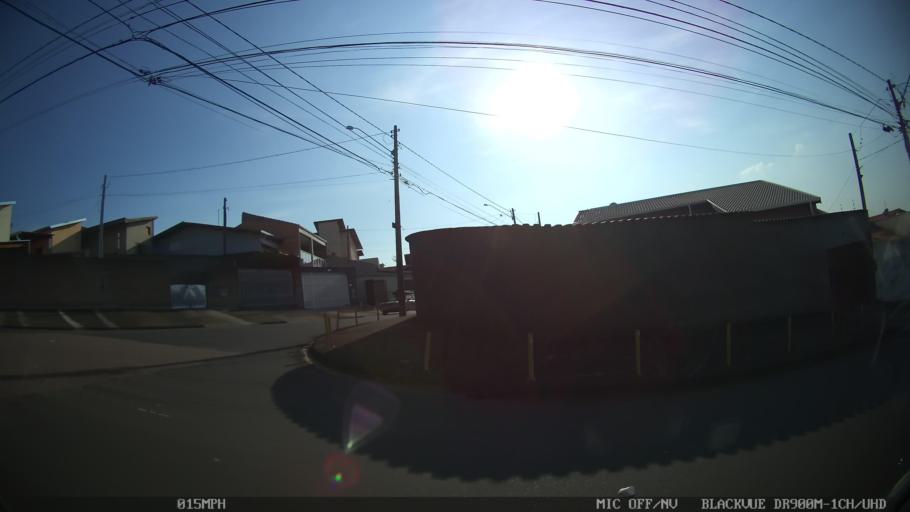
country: BR
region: Sao Paulo
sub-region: Campinas
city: Campinas
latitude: -22.9840
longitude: -47.1392
